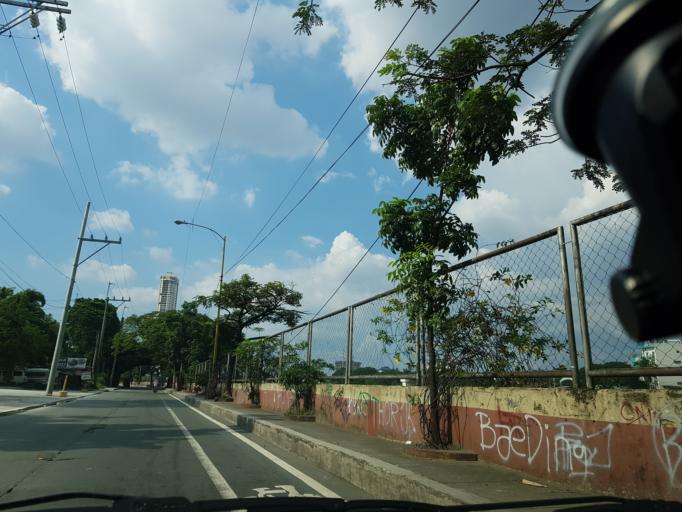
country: PH
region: Metro Manila
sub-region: Marikina
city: Calumpang
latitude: 14.5949
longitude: 121.0909
